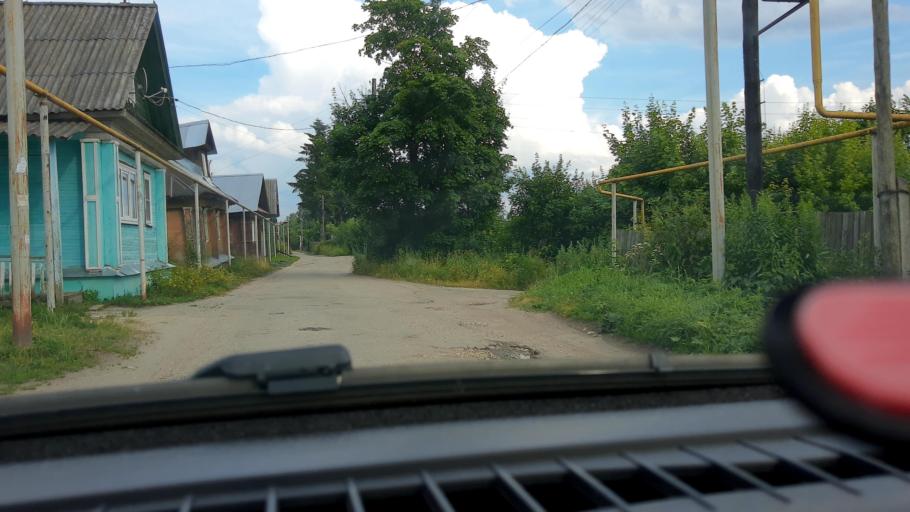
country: RU
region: Nizjnij Novgorod
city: Gorodets
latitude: 56.6169
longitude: 43.4967
